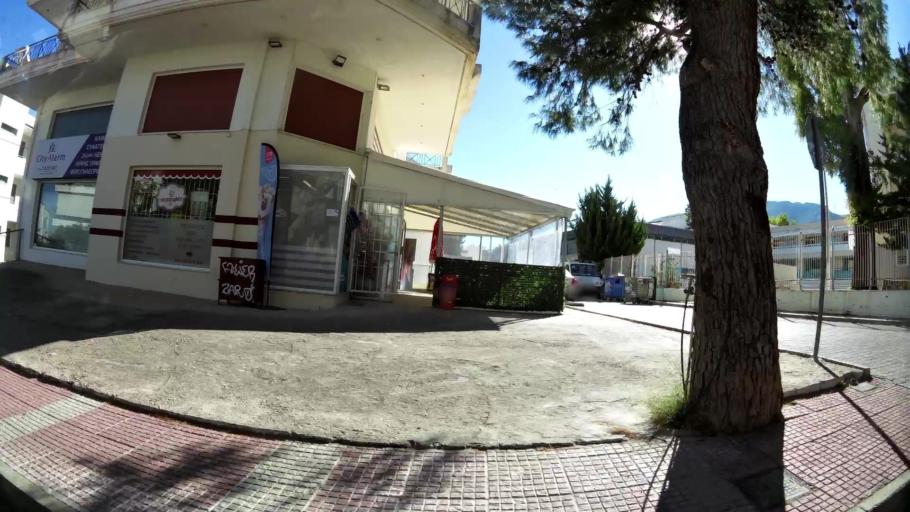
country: GR
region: Attica
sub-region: Nomarchia Anatolikis Attikis
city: Leondarion
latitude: 37.9837
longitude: 23.8468
